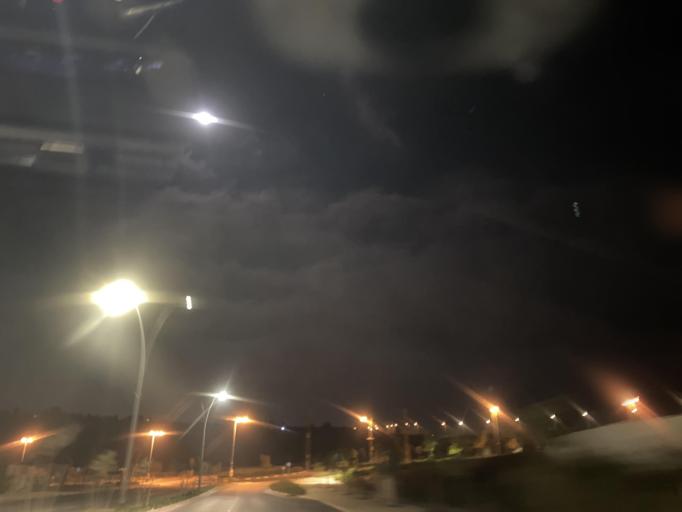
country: IL
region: Haifa
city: Daliyat el Karmil
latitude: 32.6353
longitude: 35.0779
